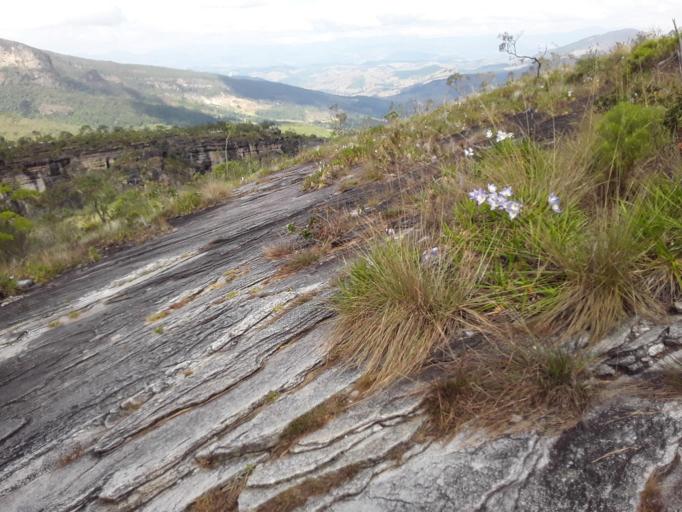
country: BR
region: Minas Gerais
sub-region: Lima Duarte
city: Lima Duarte
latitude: -21.7106
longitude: -43.8945
